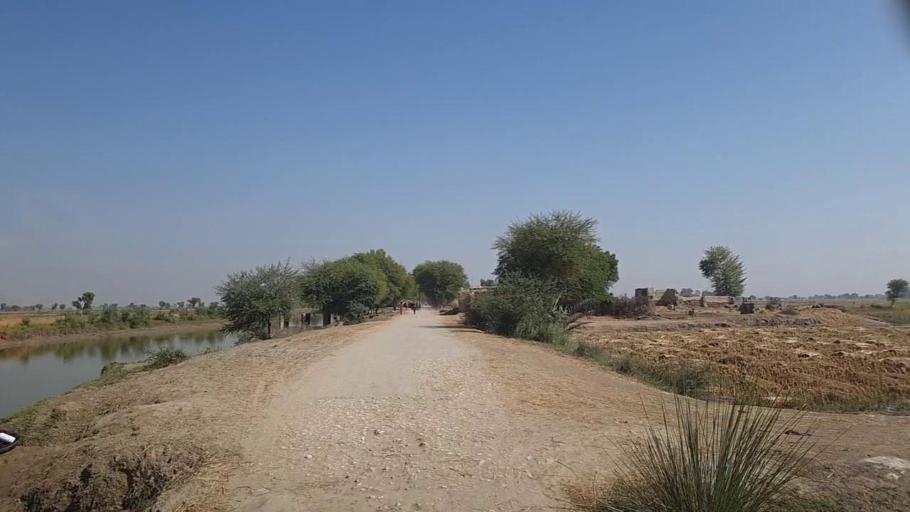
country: PK
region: Sindh
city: Thul
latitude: 28.2547
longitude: 68.8204
